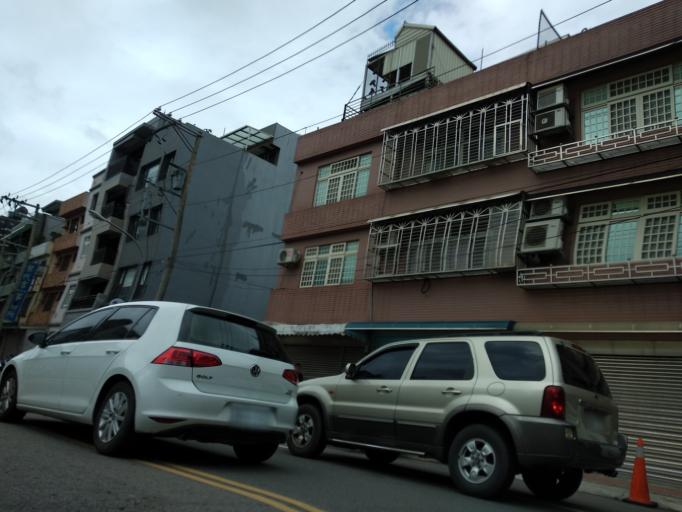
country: TW
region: Taiwan
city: Taoyuan City
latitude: 24.9647
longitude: 121.2168
